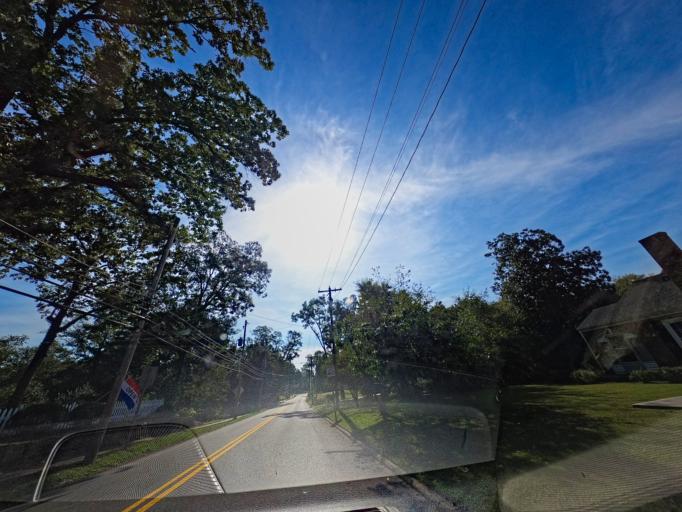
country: US
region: Georgia
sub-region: Troup County
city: Hogansville
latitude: 33.1699
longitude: -84.9062
